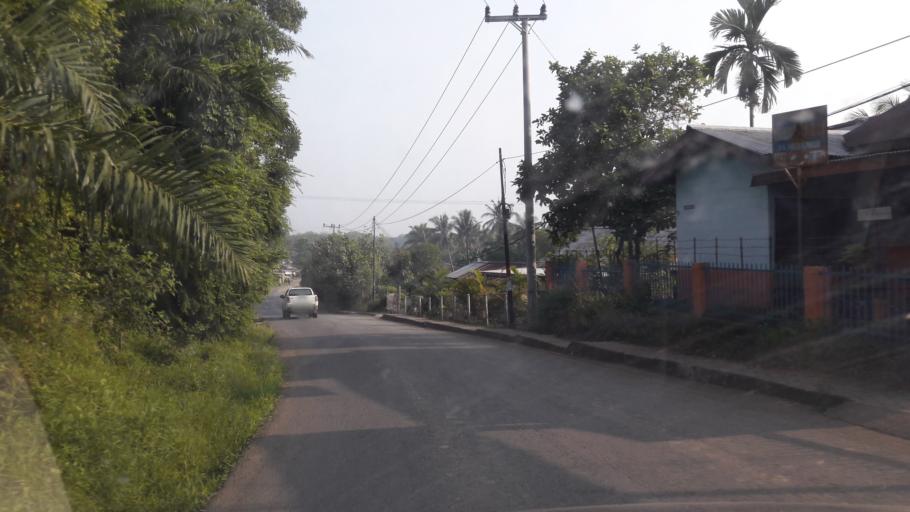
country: ID
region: South Sumatra
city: Gunungmegang Dalam
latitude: -3.2712
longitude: 103.8283
